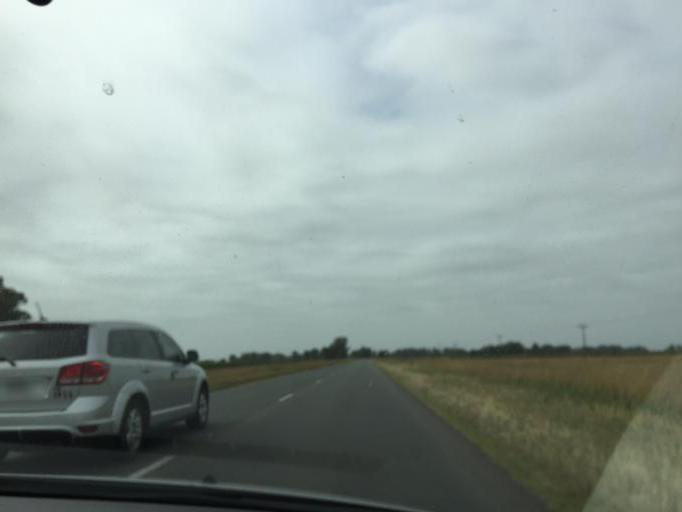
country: AR
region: Buenos Aires
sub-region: Partido de Las Flores
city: Las Flores
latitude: -36.1868
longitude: -59.0580
